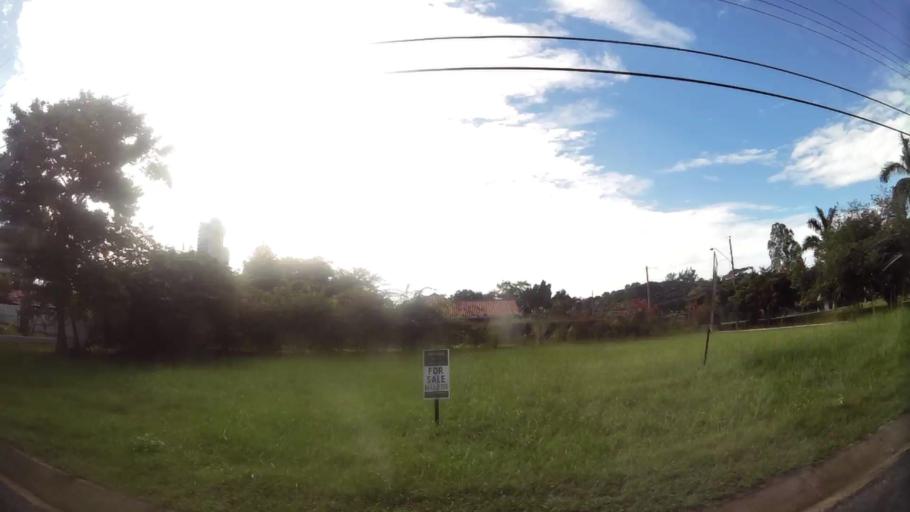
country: PA
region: Panama
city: Nueva Gorgona
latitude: 8.5407
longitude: -79.8888
